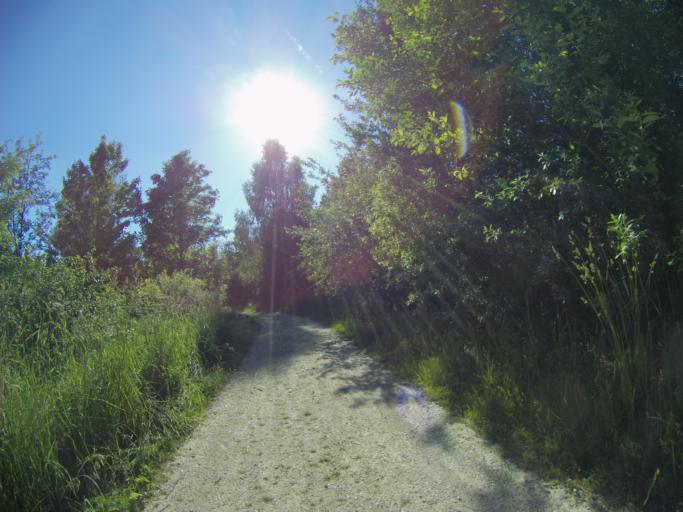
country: DE
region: Bavaria
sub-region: Upper Bavaria
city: Kirchdorf
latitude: 48.4128
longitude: 11.6696
